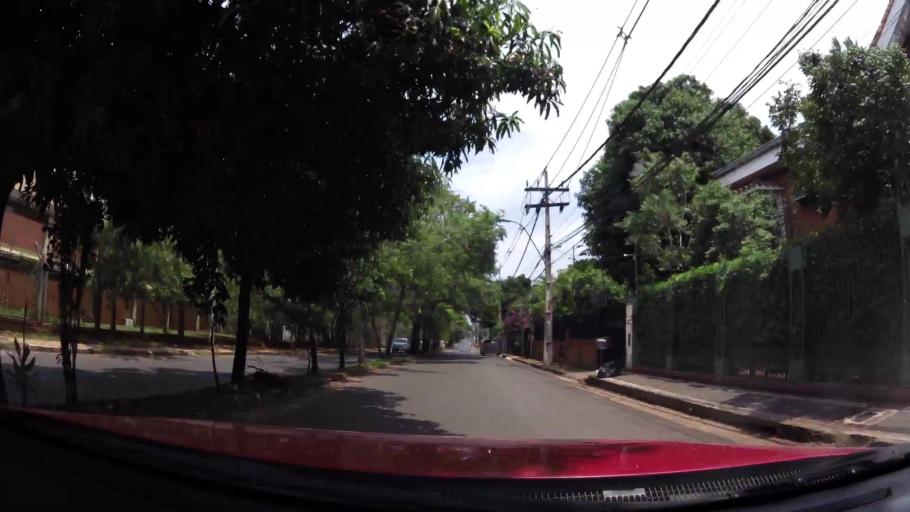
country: PY
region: Central
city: Lambare
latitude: -25.3097
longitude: -57.5685
